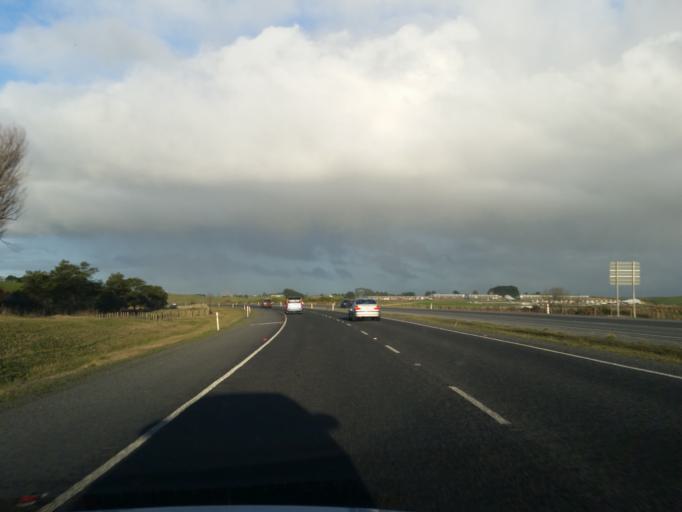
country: NZ
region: Waikato
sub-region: Waikato District
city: Te Kauwhata
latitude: -37.3452
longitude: 175.0695
